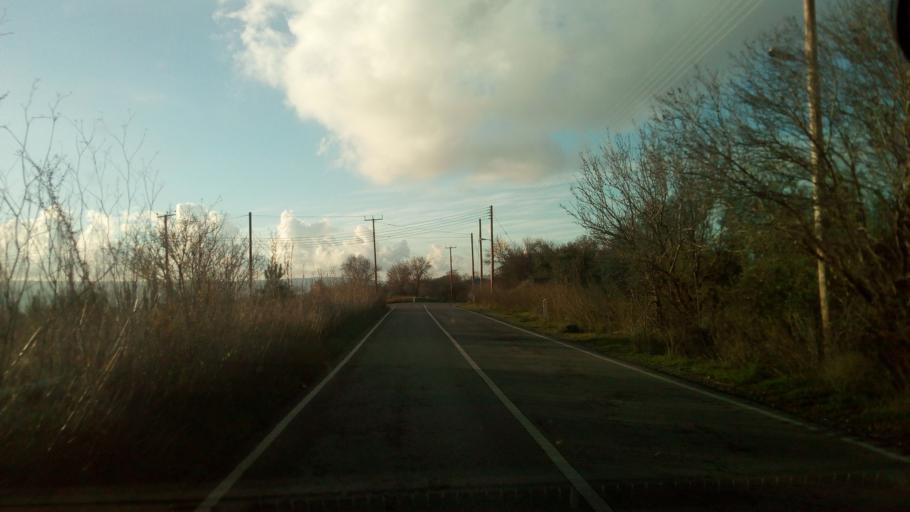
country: CY
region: Pafos
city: Tala
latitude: 34.9196
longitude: 32.5278
